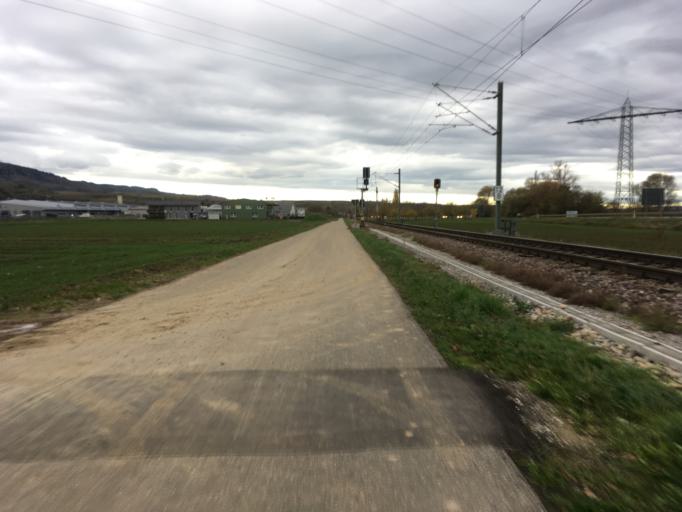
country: DE
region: Baden-Wuerttemberg
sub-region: Freiburg Region
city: Gottenheim
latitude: 48.0579
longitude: 7.7236
